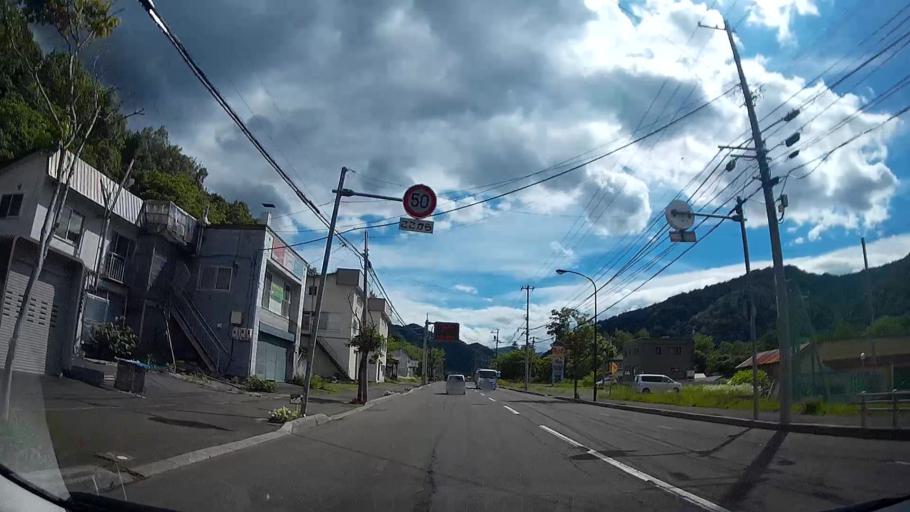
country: JP
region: Hokkaido
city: Sapporo
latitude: 42.9617
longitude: 141.1590
